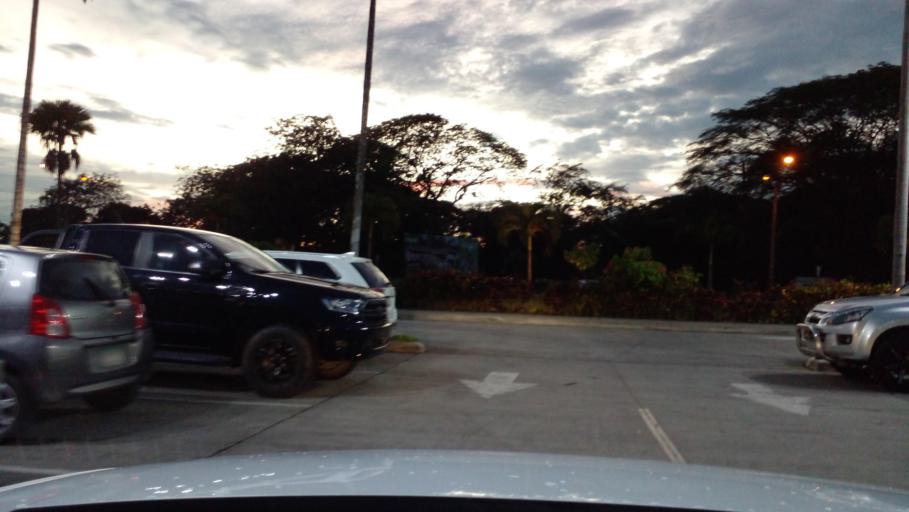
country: PA
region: Chiriqui
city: David
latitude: 8.4358
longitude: -82.4384
